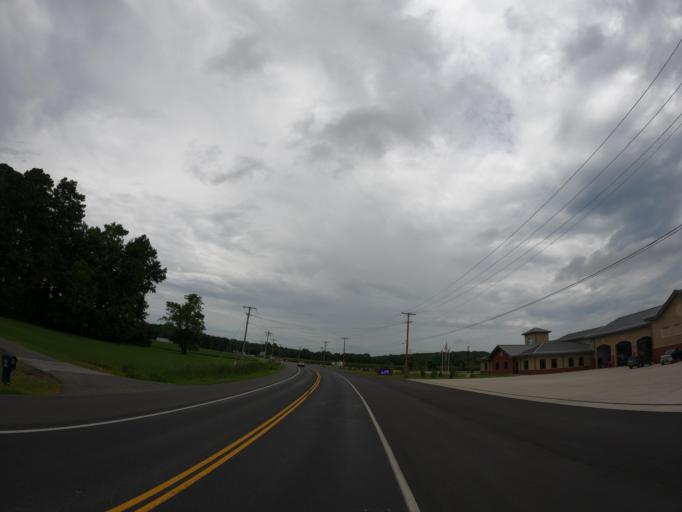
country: US
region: Maryland
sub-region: Saint Mary's County
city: Lexington Park
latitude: 38.1897
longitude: -76.5126
